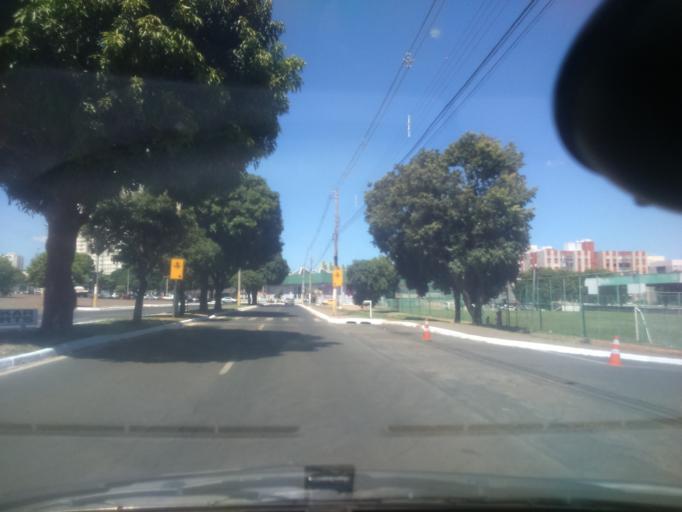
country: BR
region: Goias
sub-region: Luziania
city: Luziania
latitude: -16.0112
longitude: -48.0639
